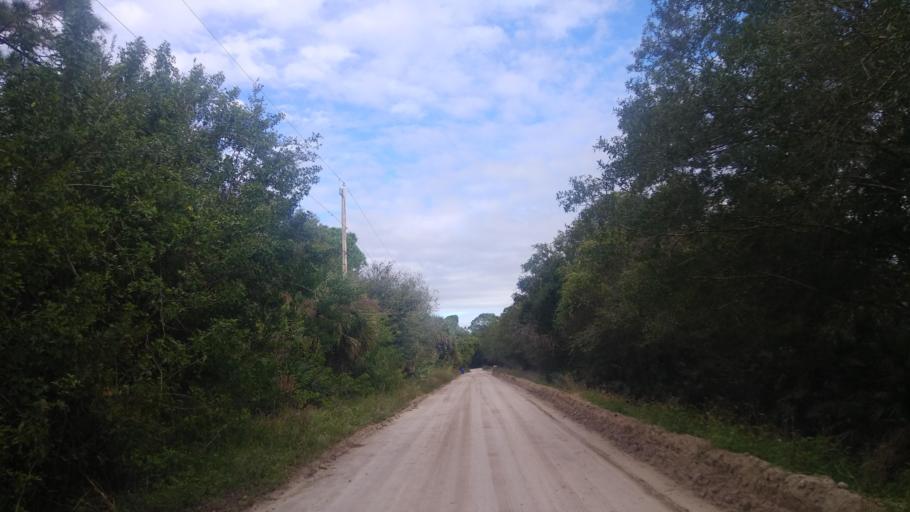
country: US
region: Florida
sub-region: Indian River County
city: Fellsmere
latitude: 27.7609
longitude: -80.5797
